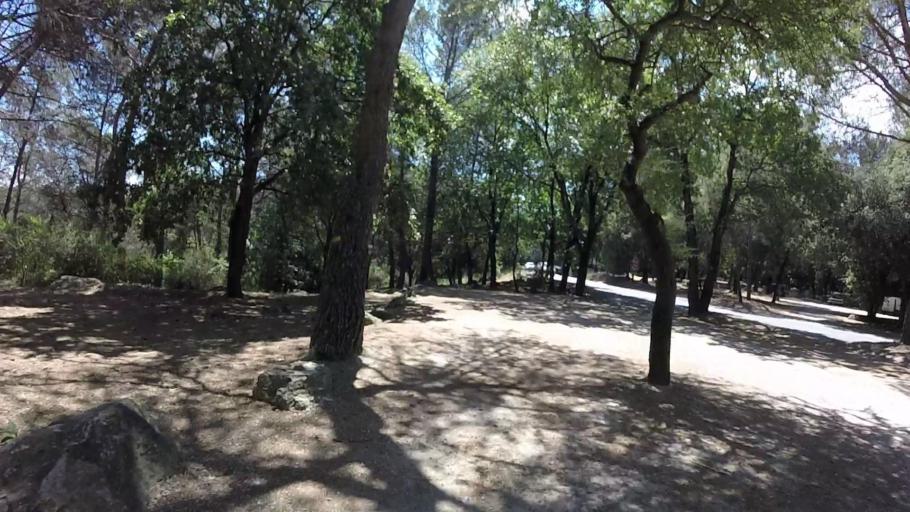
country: FR
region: Provence-Alpes-Cote d'Azur
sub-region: Departement des Alpes-Maritimes
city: Vallauris
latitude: 43.5978
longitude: 7.0370
